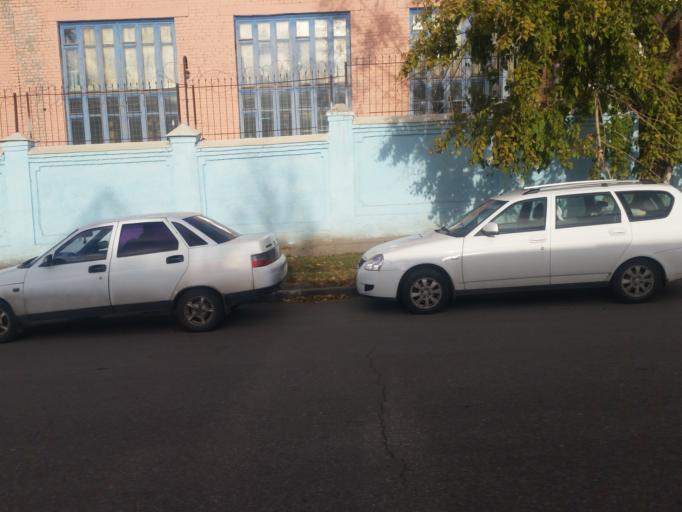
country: RU
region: Ulyanovsk
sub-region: Ulyanovskiy Rayon
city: Ulyanovsk
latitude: 54.3177
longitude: 48.3871
